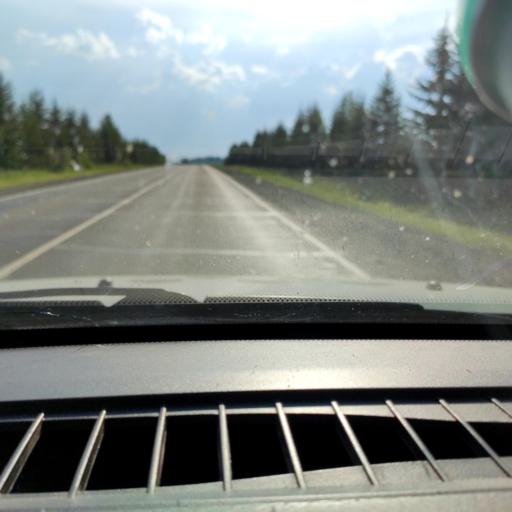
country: RU
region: Udmurtiya
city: Debesy
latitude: 57.6797
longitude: 53.9279
